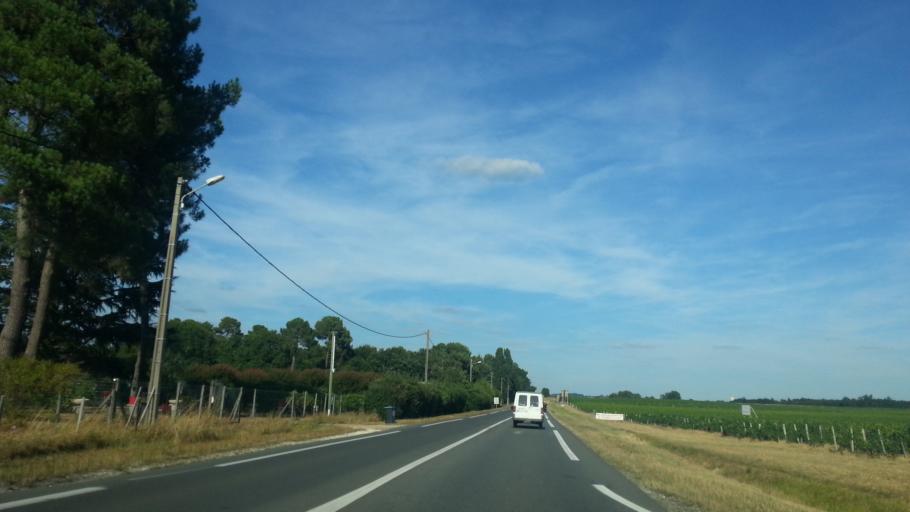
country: FR
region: Aquitaine
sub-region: Departement de la Gironde
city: Ayguemorte-les-Graves
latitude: 44.6967
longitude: -0.4809
